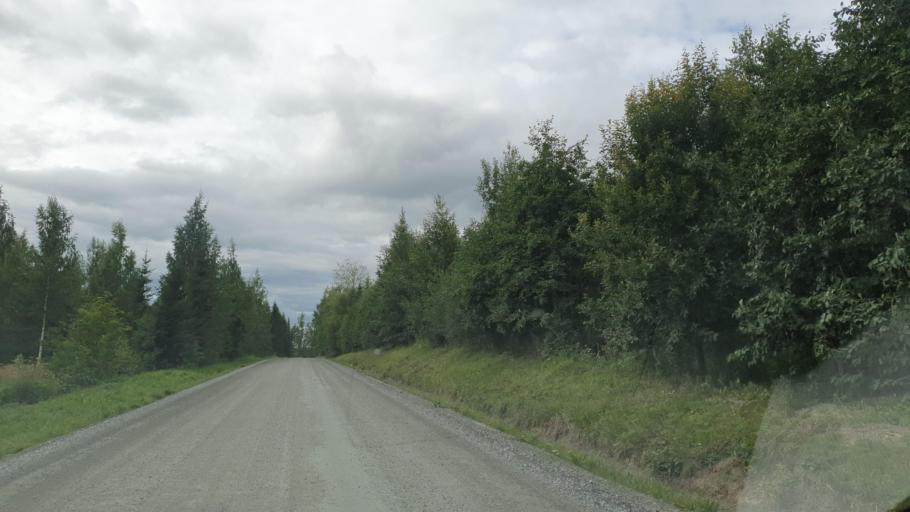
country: FI
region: Northern Savo
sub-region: Ylae-Savo
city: Iisalmi
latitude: 63.5170
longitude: 27.1067
